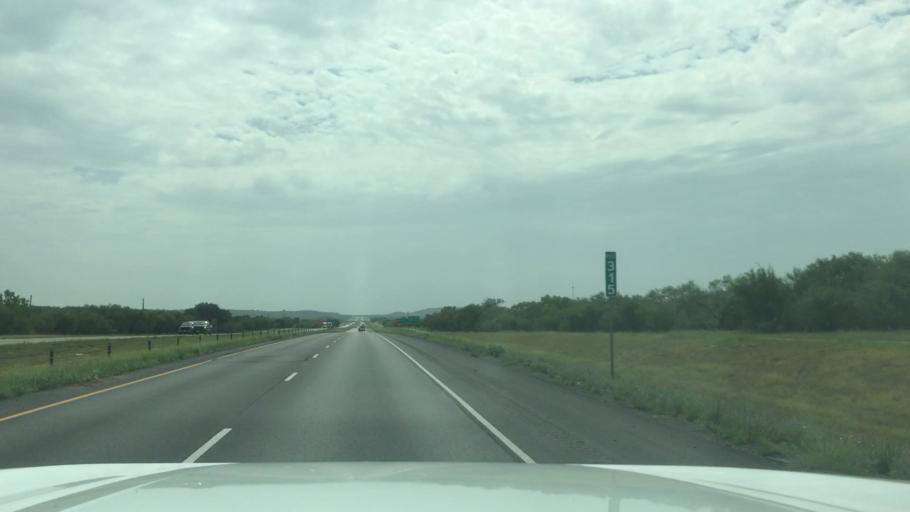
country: US
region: Texas
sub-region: Callahan County
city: Baird
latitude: 32.3802
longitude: -99.2667
